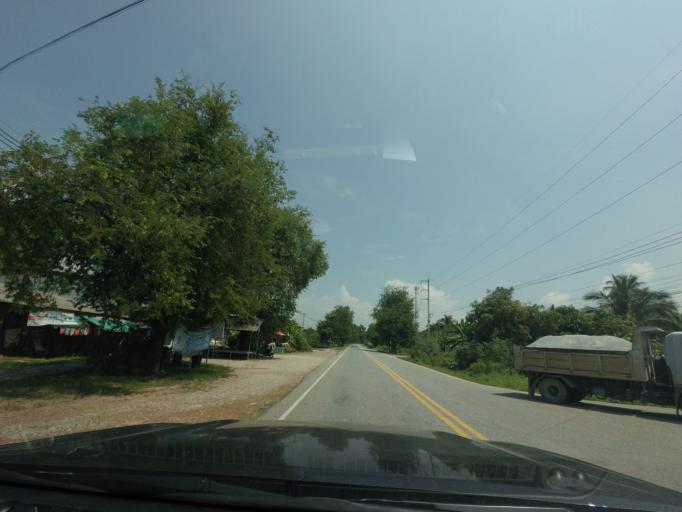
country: TH
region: Uttaradit
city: Thong Saen Khan
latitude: 17.4650
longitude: 100.2805
